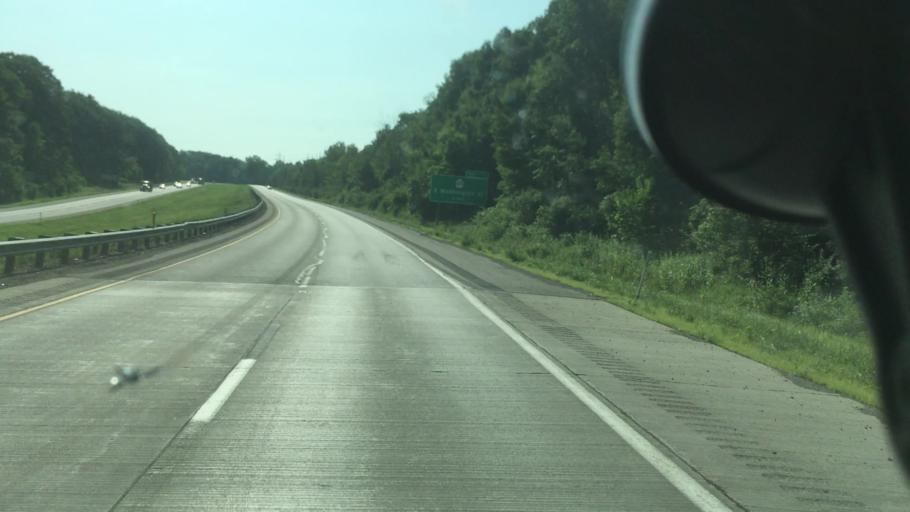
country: US
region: Pennsylvania
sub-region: Lawrence County
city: New Castle
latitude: 40.9683
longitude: -80.3363
